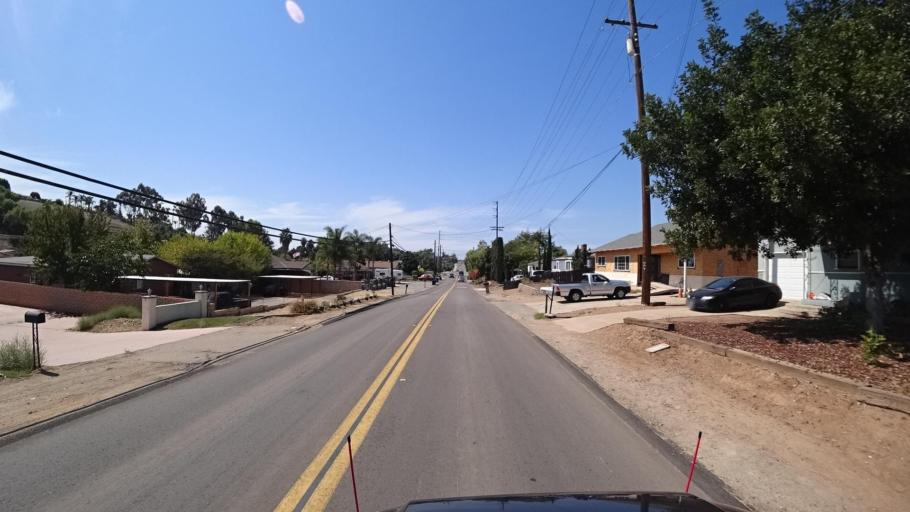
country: US
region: California
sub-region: San Diego County
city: Bonita
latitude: 32.6773
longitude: -117.0059
